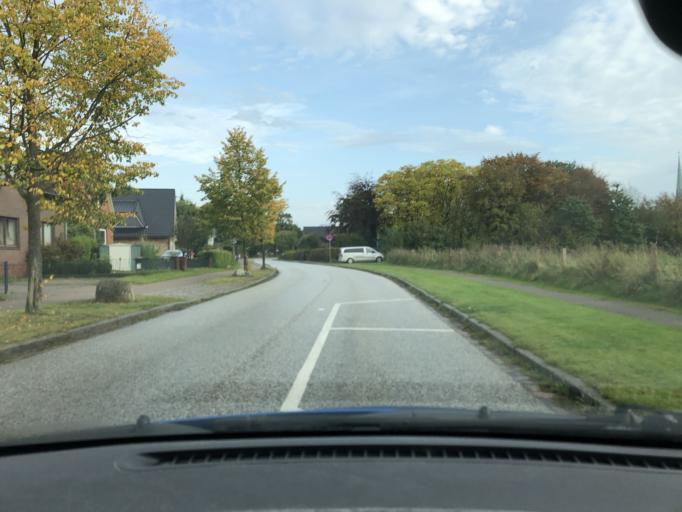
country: DE
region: Schleswig-Holstein
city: Siek
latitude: 53.6366
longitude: 10.2934
